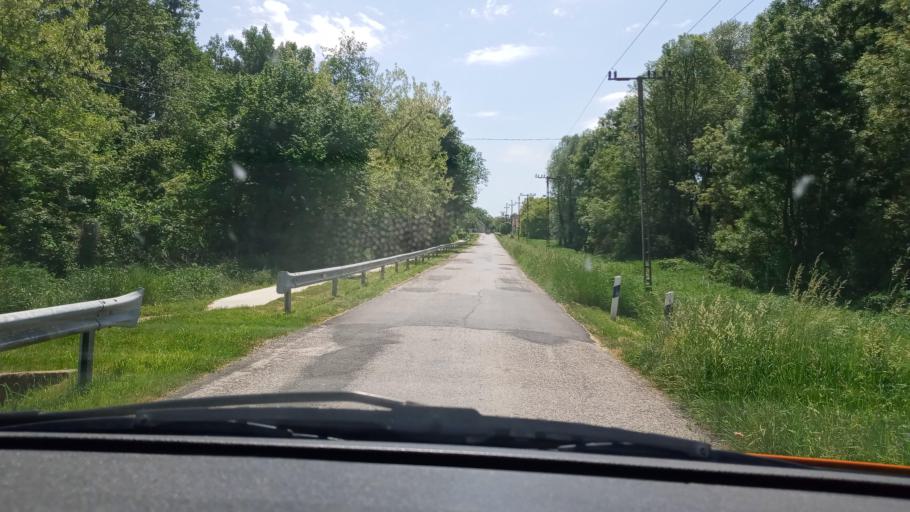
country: HU
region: Baranya
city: Harkany
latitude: 45.8380
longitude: 18.2048
